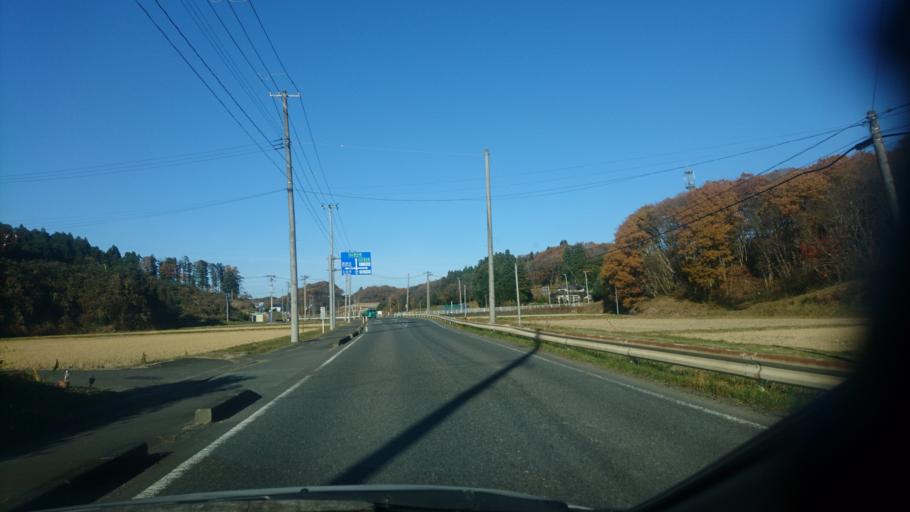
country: JP
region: Miyagi
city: Tomiya
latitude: 38.4602
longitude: 140.9046
